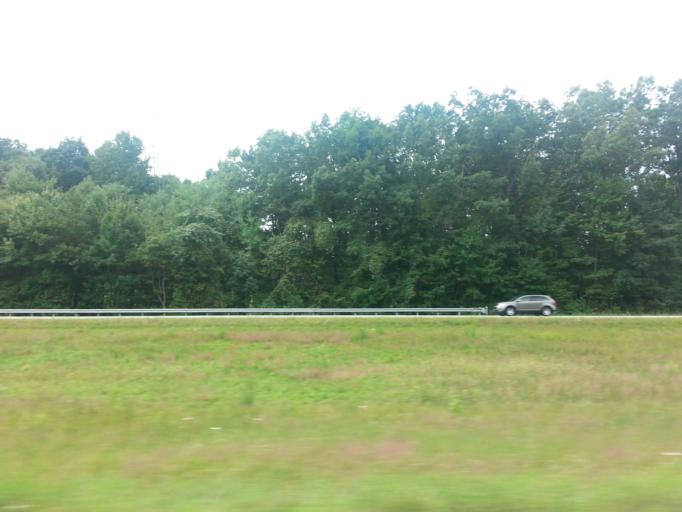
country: US
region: Tennessee
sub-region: Roane County
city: Rockwood
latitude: 35.8972
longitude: -84.7628
